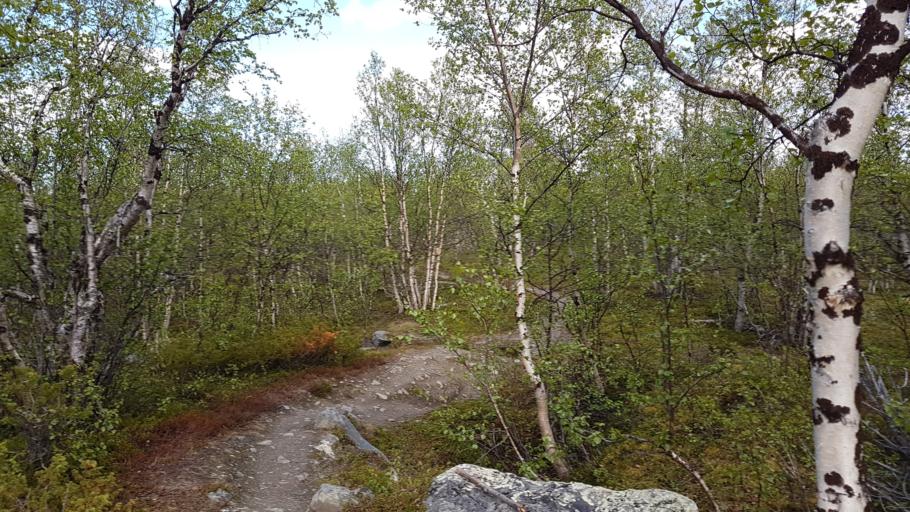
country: NO
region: Troms
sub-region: Bardu
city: Setermoen
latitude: 68.3408
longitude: 18.7683
